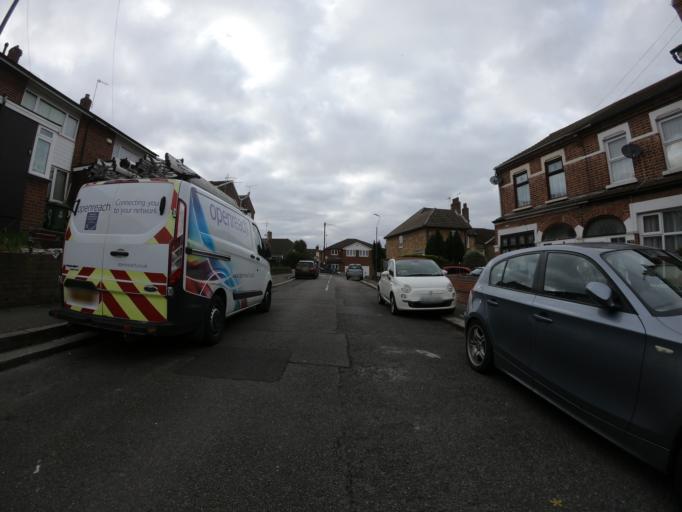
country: GB
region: England
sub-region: Greater London
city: Belvedere
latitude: 51.4893
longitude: 0.1470
